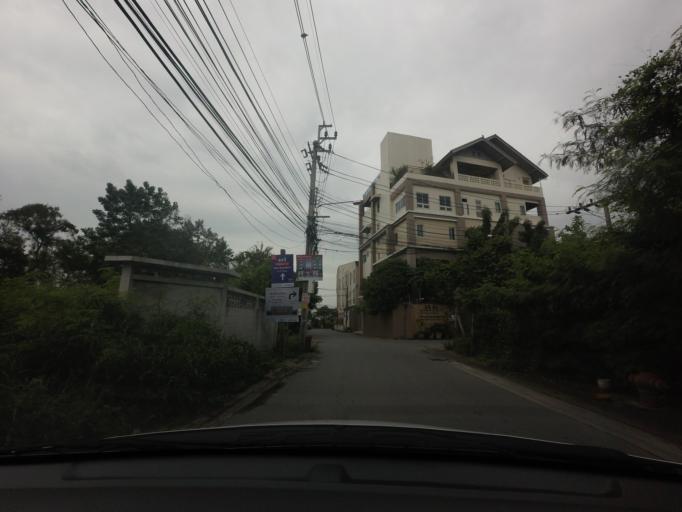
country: TH
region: Bangkok
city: Lak Si
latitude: 13.8954
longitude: 100.5689
